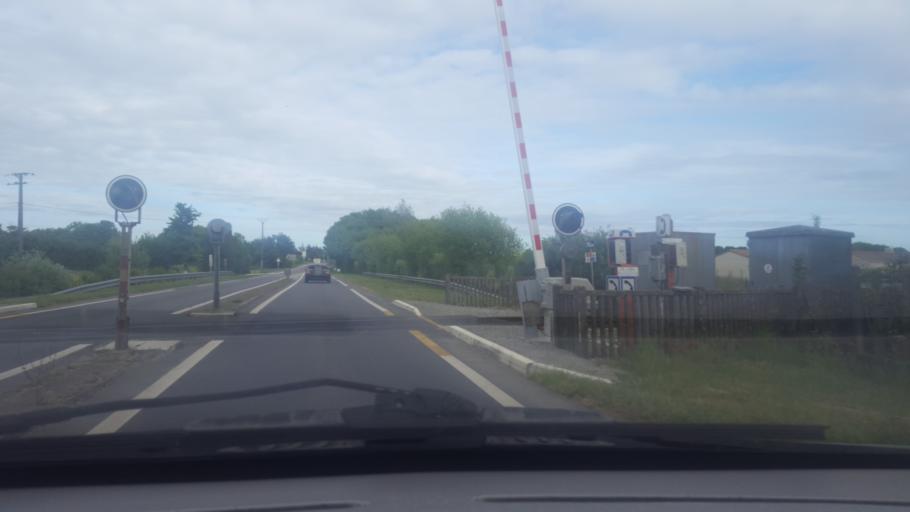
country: FR
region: Pays de la Loire
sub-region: Departement de la Loire-Atlantique
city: Machecoul
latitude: 47.0027
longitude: -1.8301
